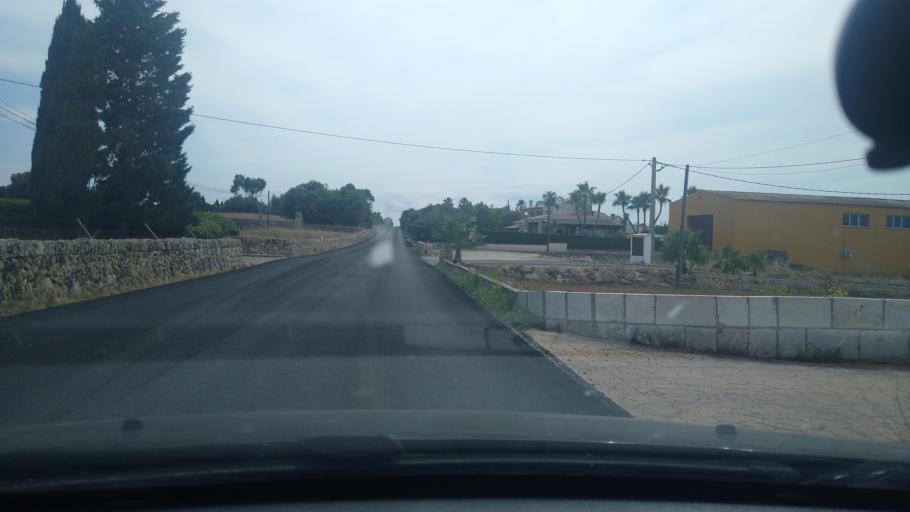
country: ES
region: Balearic Islands
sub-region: Illes Balears
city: Santa Margalida
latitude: 39.7397
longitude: 3.1235
